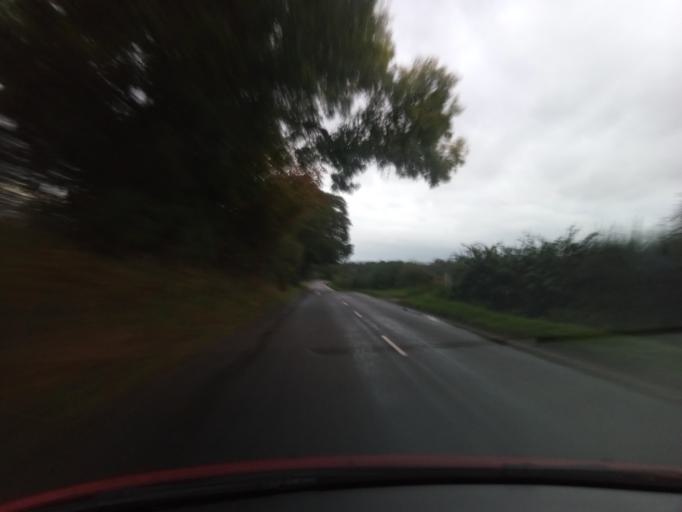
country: GB
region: England
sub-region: Darlington
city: High Coniscliffe
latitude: 54.5293
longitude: -1.6722
